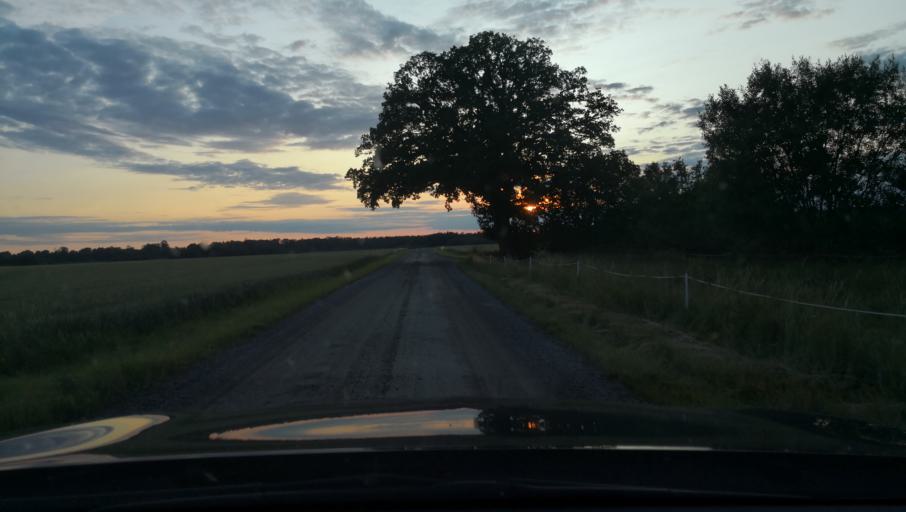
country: SE
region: Uppsala
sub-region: Osthammars Kommun
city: Bjorklinge
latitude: 60.0553
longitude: 17.5966
